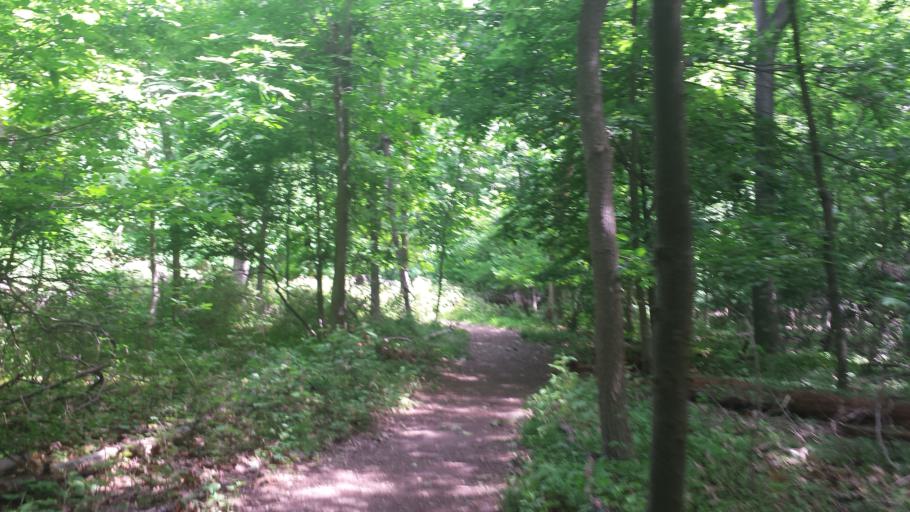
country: US
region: New York
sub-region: Westchester County
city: Harrison
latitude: 40.9529
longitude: -73.7023
